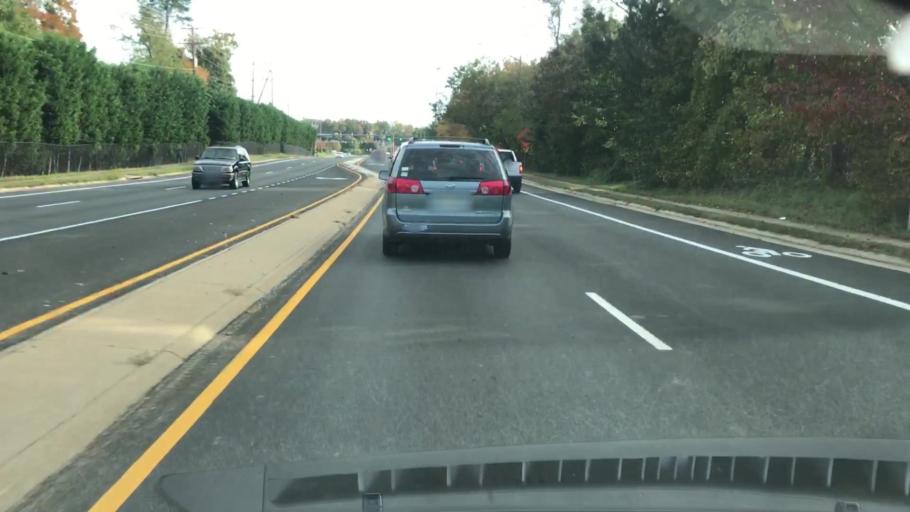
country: US
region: Virginia
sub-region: Fairfax County
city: Newington
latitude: 38.7451
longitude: -77.1665
